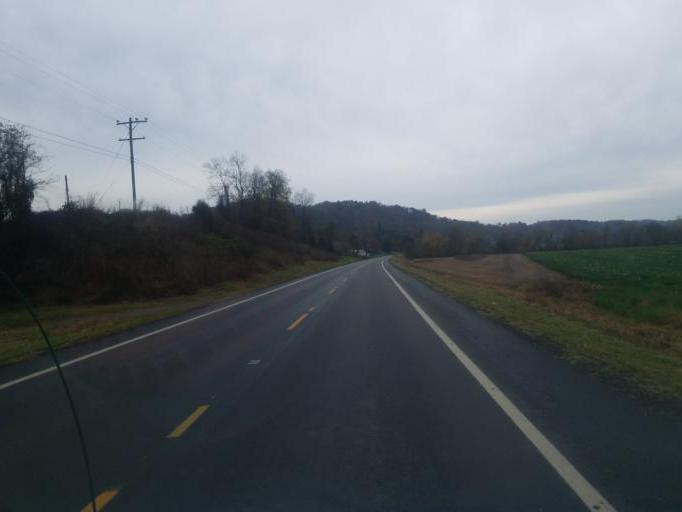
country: US
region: Ohio
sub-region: Washington County
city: Beverly
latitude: 39.5562
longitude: -81.5581
